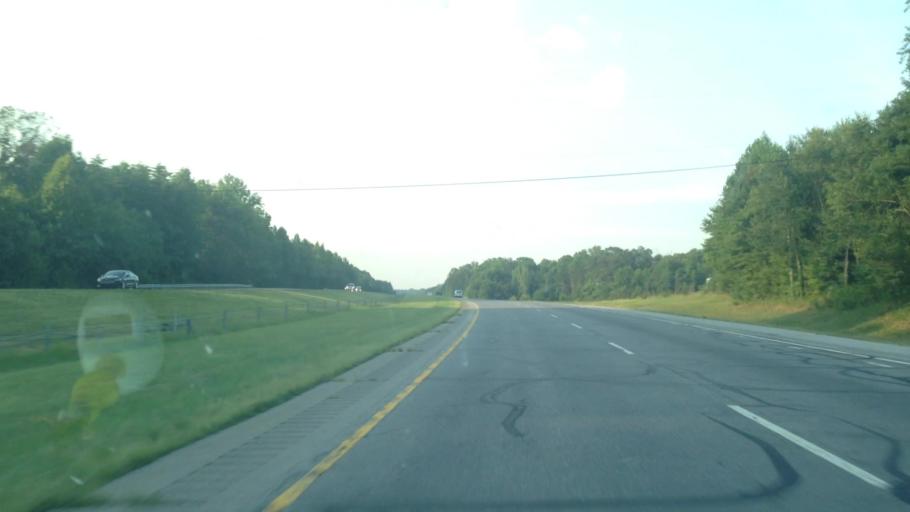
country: US
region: Virginia
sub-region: City of Danville
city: Danville
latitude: 36.4918
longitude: -79.4856
